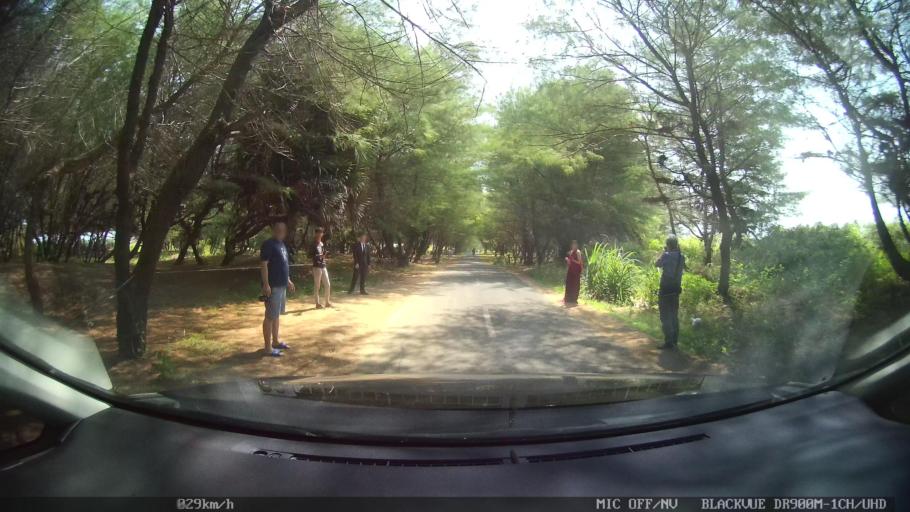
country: ID
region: Daerah Istimewa Yogyakarta
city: Bambanglipuro
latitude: -8.0166
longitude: 110.3057
